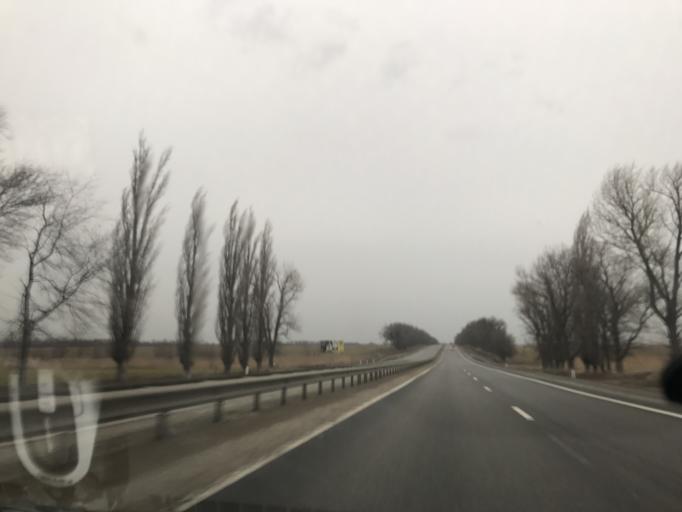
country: RU
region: Krasnodarskiy
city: Pavlovskaya
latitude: 46.1663
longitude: 39.8415
